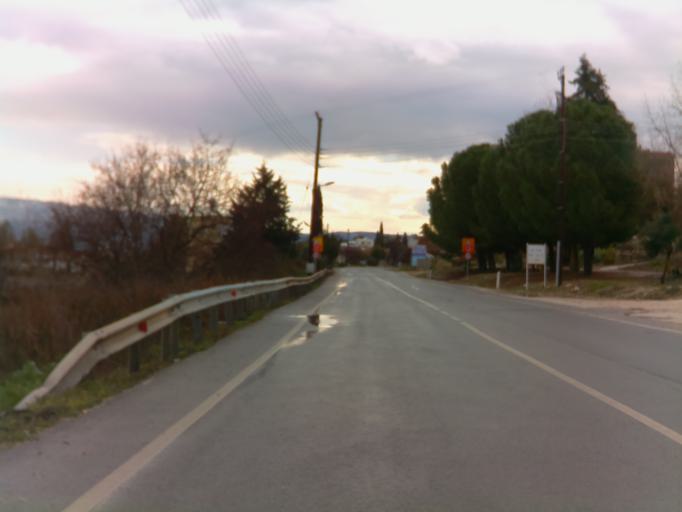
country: CY
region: Pafos
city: Tala
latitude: 34.8917
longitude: 32.4742
